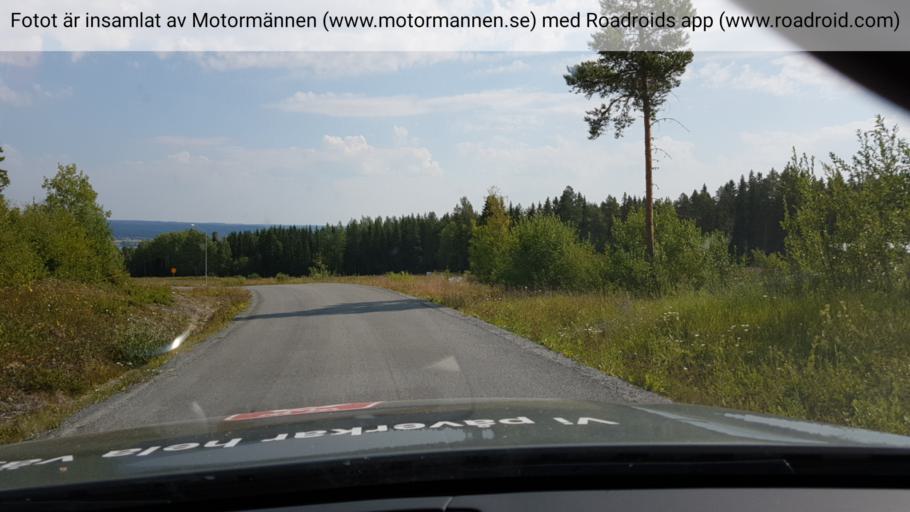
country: SE
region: Jaemtland
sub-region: OEstersunds Kommun
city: Ostersund
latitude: 63.1239
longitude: 14.6354
